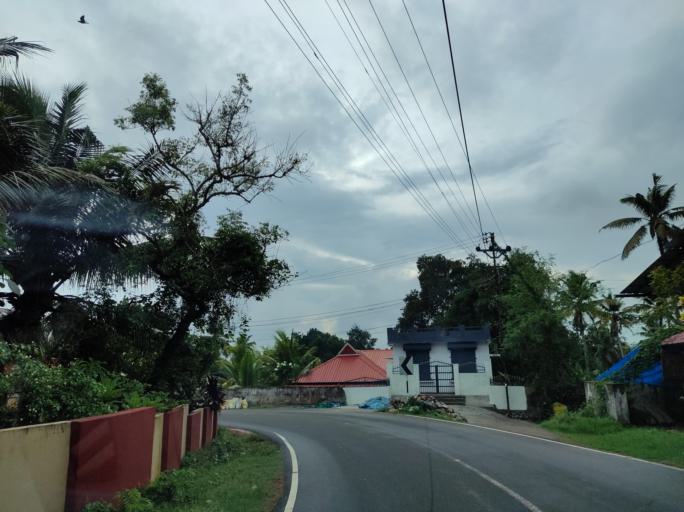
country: IN
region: Kerala
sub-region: Alappuzha
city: Mavelikara
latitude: 9.2279
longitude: 76.5760
